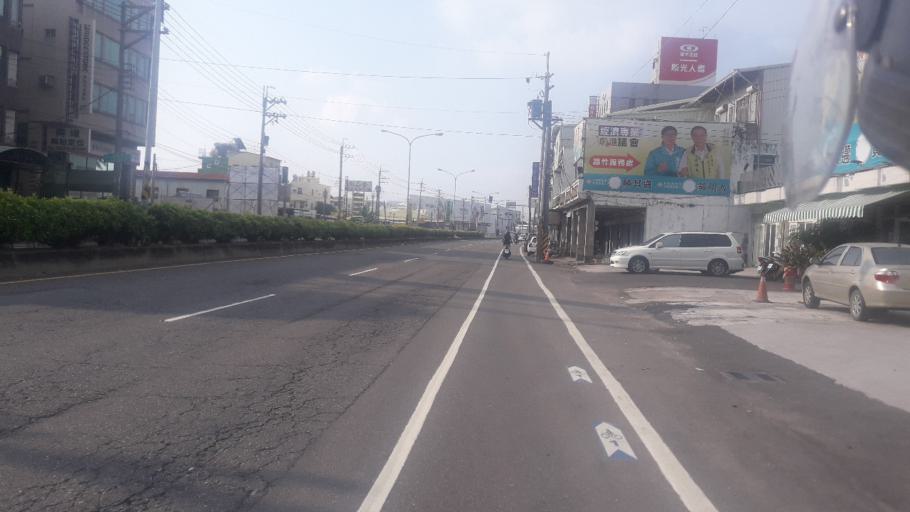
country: TW
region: Taiwan
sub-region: Tainan
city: Tainan
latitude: 22.8634
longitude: 120.2578
